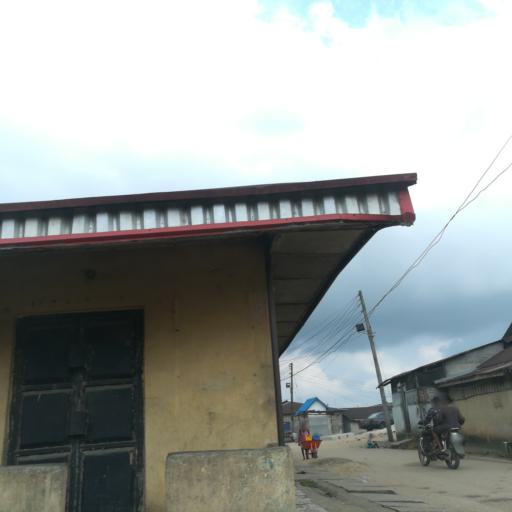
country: NG
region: Rivers
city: Okrika
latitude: 4.7942
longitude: 7.1223
